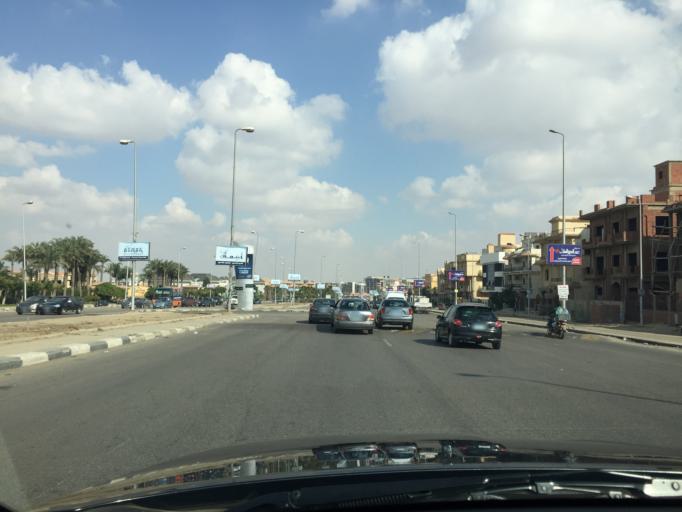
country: EG
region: Muhafazat al Qahirah
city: Cairo
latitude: 30.0207
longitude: 31.4510
